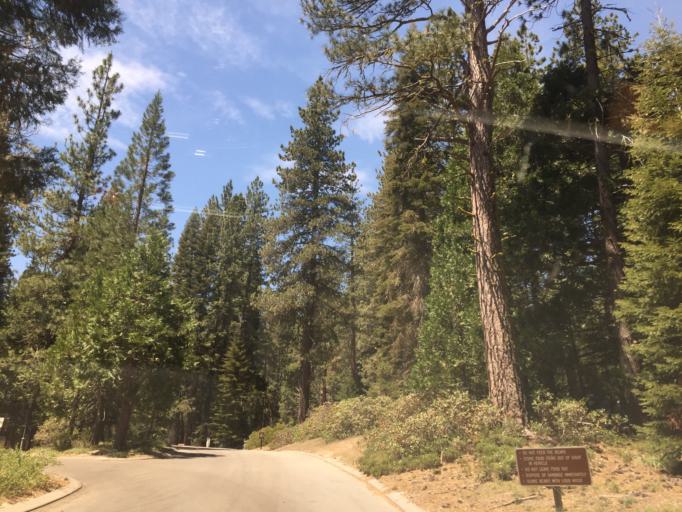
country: US
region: California
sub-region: Fresno County
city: Squaw Valley
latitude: 36.8027
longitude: -118.9401
